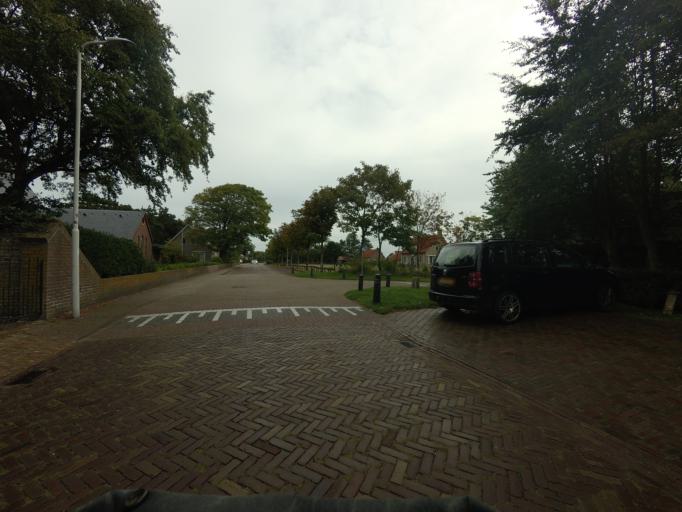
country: NL
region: Friesland
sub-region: Gemeente Ameland
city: Nes
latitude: 53.4464
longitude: 5.7782
